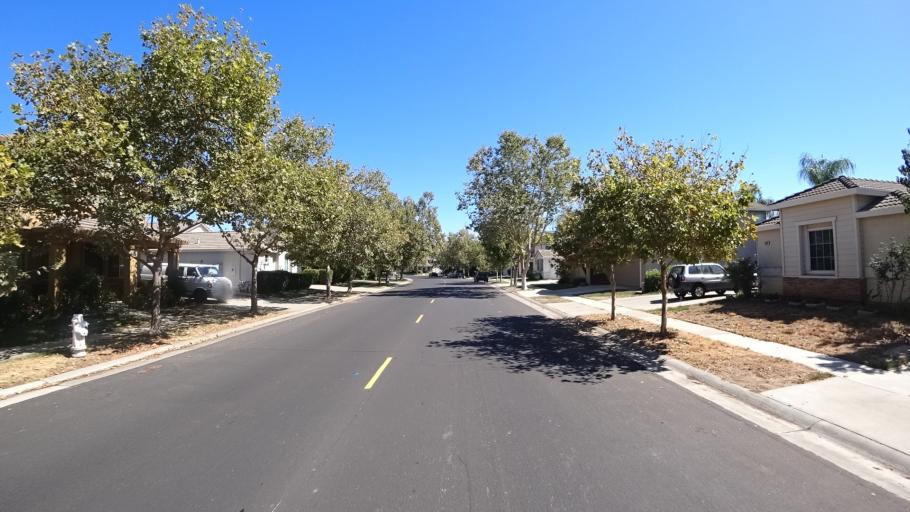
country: US
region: California
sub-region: Sacramento County
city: Laguna
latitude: 38.4172
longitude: -121.4736
